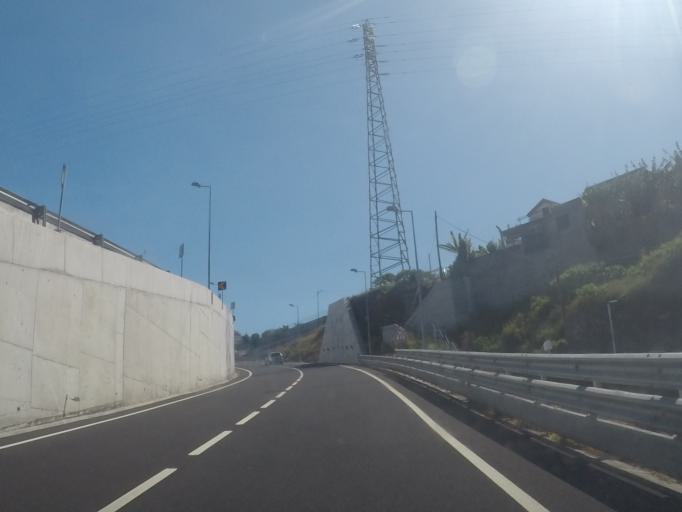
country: PT
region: Madeira
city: Camara de Lobos
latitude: 32.6602
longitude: -16.9685
